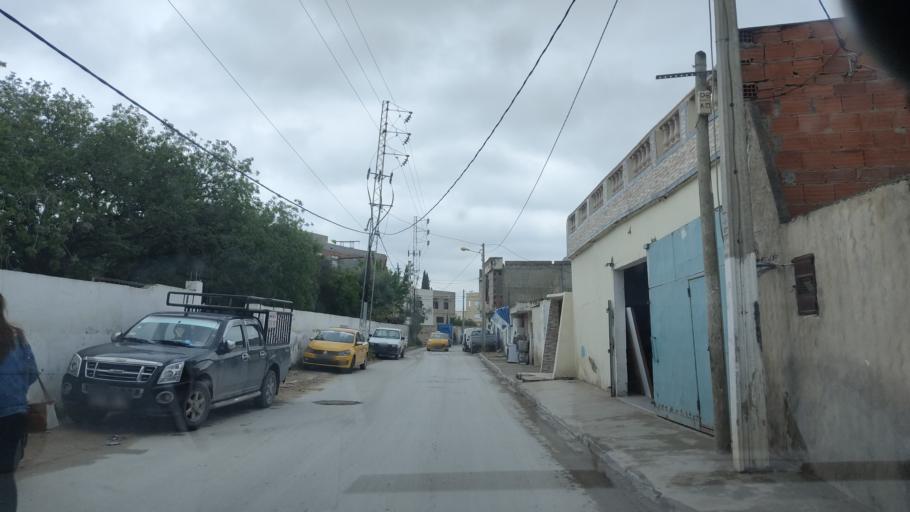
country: TN
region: Ariana
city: Ariana
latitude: 36.8779
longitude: 10.2175
